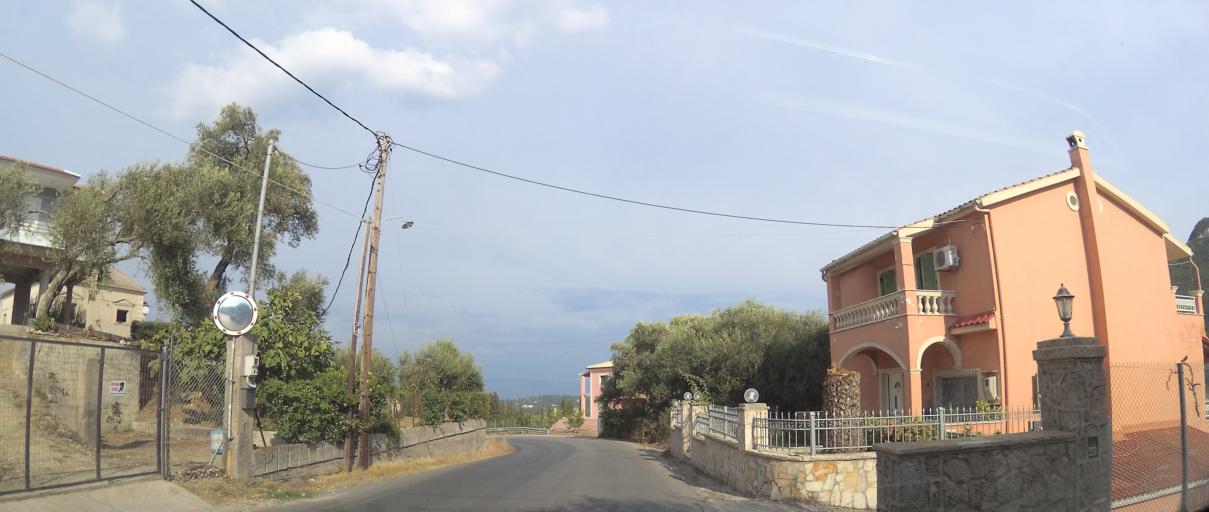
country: GR
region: Ionian Islands
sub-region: Nomos Kerkyras
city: Kynopiastes
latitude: 39.5626
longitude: 19.8682
